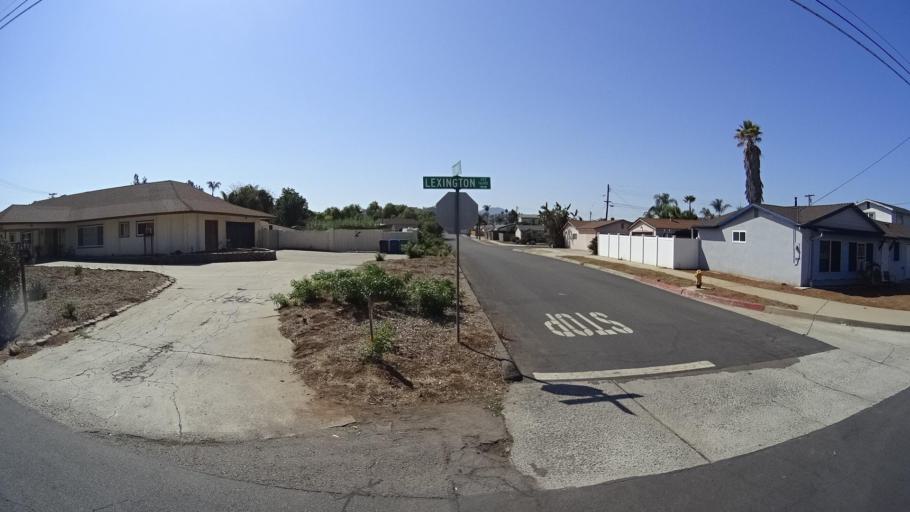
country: US
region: California
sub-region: San Diego County
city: Granite Hills
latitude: 32.7927
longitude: -116.9215
